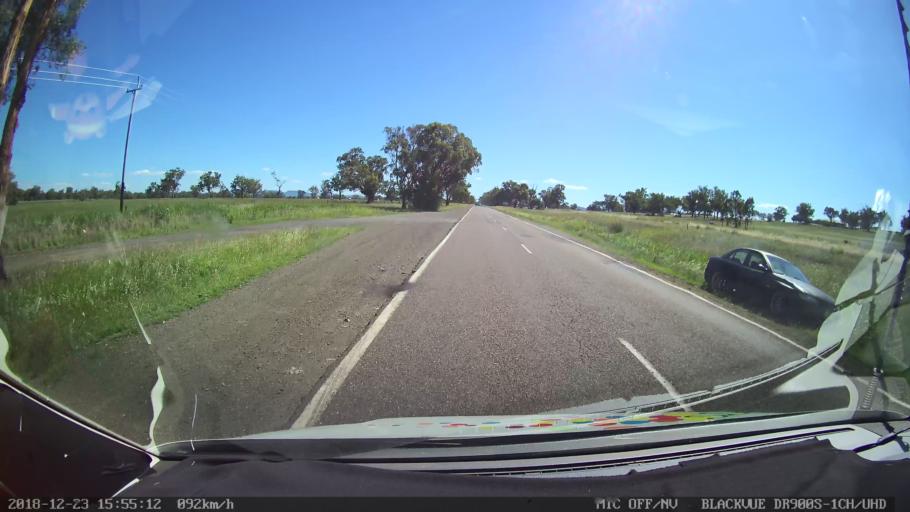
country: AU
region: New South Wales
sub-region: Tamworth Municipality
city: Phillip
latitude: -31.1531
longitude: 150.8708
